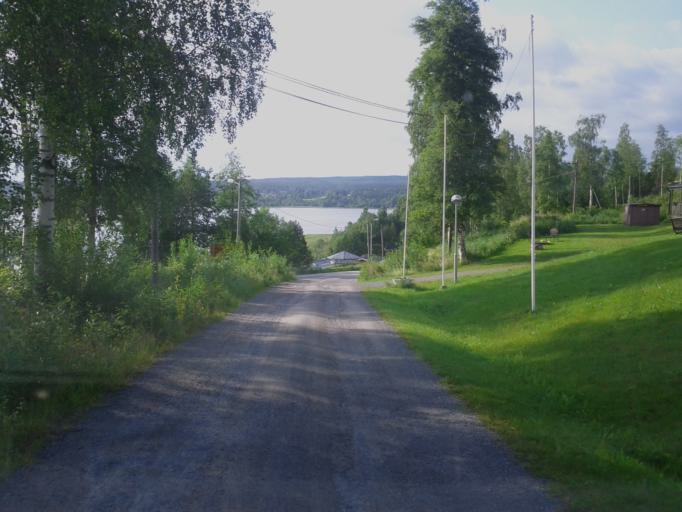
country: SE
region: Vaesternorrland
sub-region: OErnskoeldsviks Kommun
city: Ornskoldsvik
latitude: 63.2570
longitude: 18.8103
